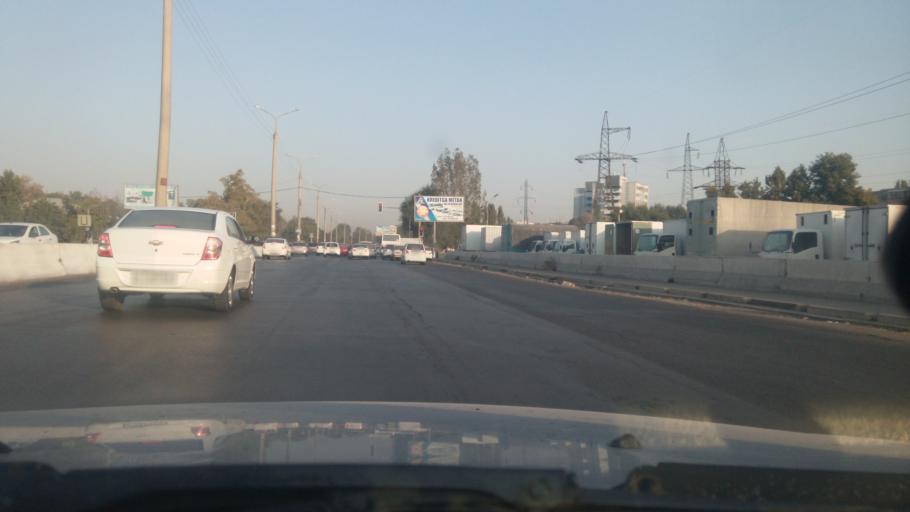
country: UZ
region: Toshkent Shahri
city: Tashkent
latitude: 41.2546
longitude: 69.1579
